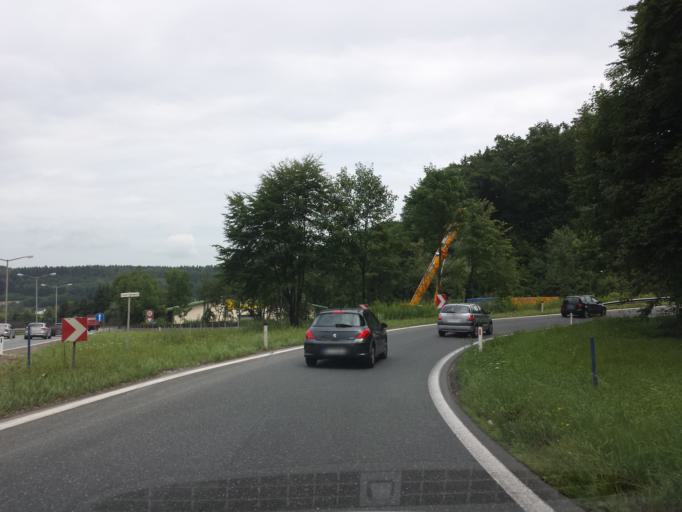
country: AT
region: Salzburg
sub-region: Politischer Bezirk Salzburg-Umgebung
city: Bergheim
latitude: 47.8336
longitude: 13.0572
